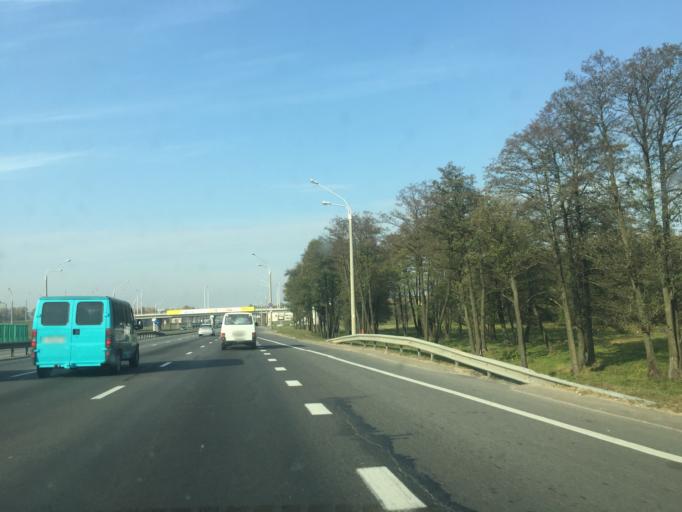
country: BY
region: Minsk
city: Vyaliki Trastsyanets
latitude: 53.8446
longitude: 27.7132
